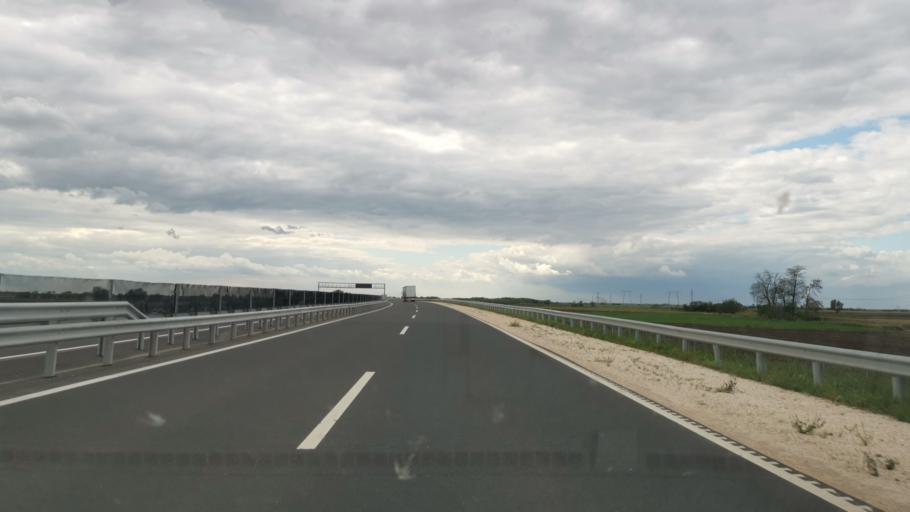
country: HU
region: Jasz-Nagykun-Szolnok
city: Zagyvarekas
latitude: 47.2087
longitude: 20.0975
